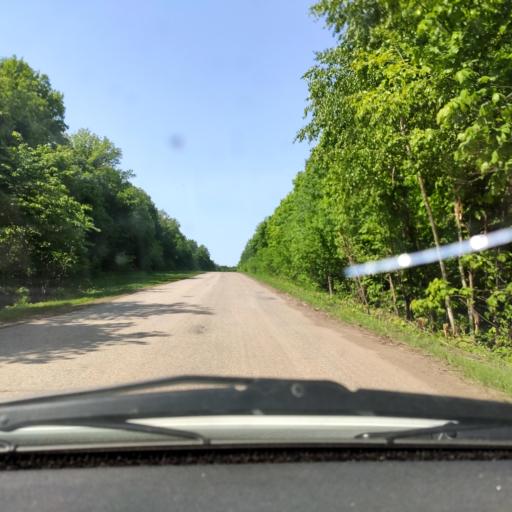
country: RU
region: Bashkortostan
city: Chishmy
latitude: 54.4521
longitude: 55.5470
